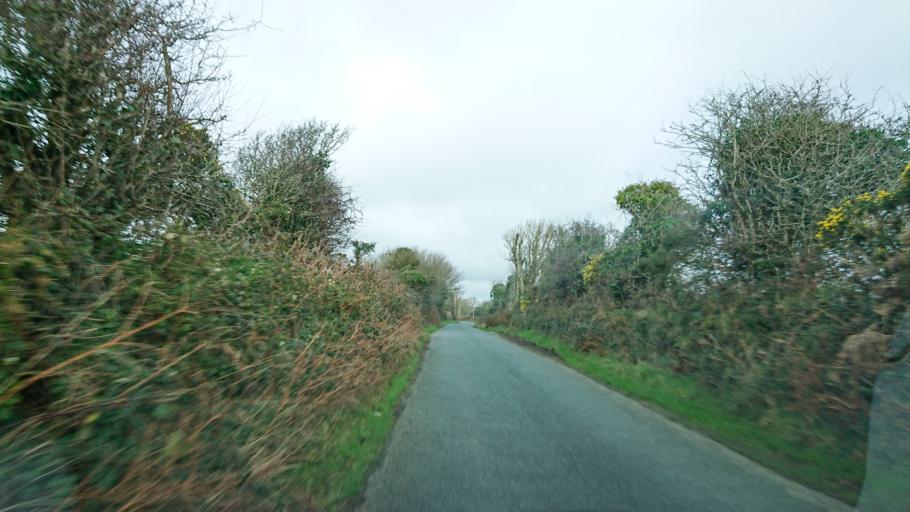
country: IE
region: Munster
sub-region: Waterford
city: Portlaw
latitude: 52.1608
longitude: -7.3067
